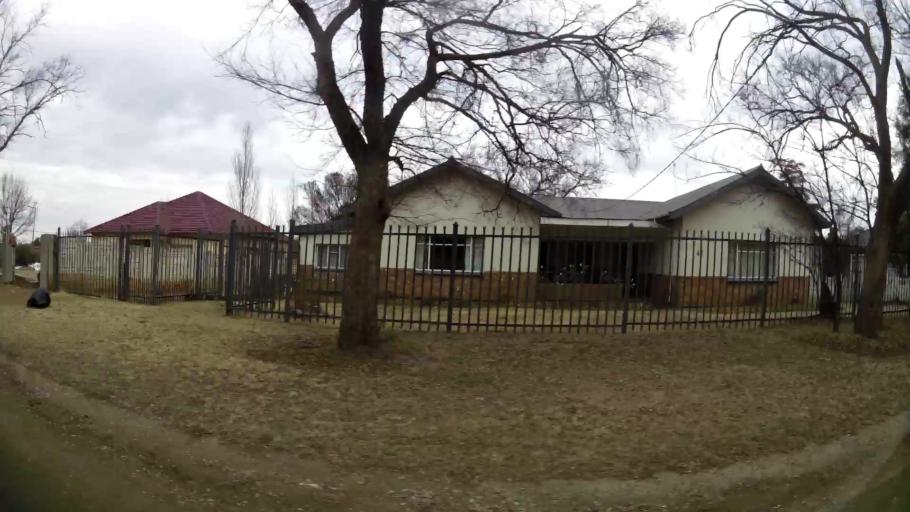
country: ZA
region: Orange Free State
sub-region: Fezile Dabi District Municipality
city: Kroonstad
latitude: -27.6859
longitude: 27.2313
